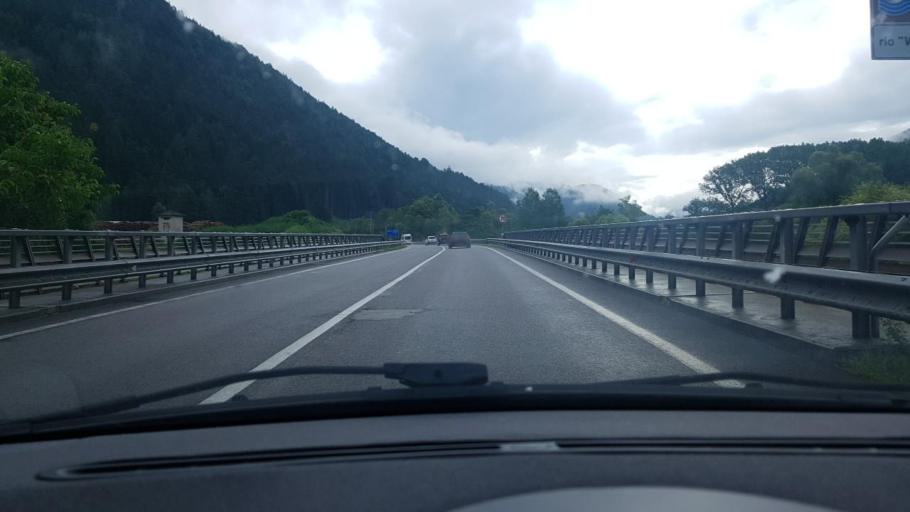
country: IT
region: Trentino-Alto Adige
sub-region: Bolzano
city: Terento
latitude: 46.8100
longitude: 11.7740
